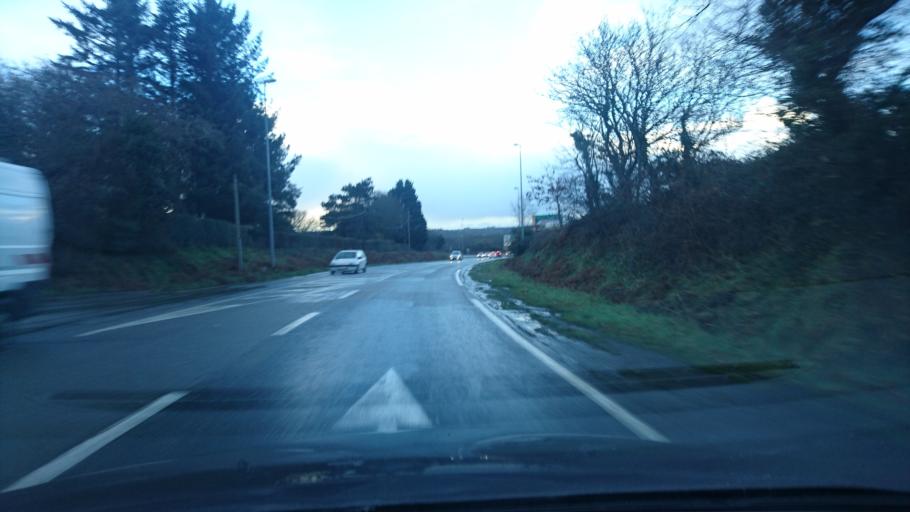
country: FR
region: Brittany
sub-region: Departement du Finistere
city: Guilers
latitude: 48.3930
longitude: -4.5394
